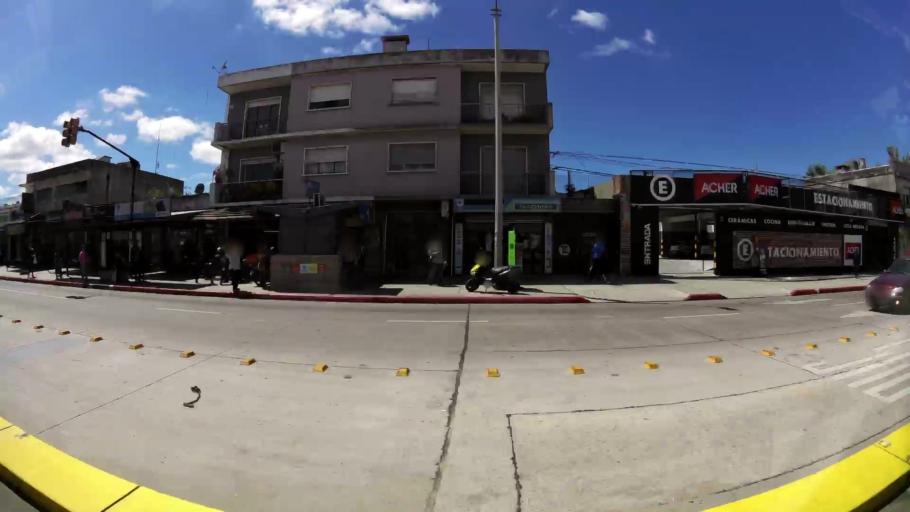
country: UY
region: Montevideo
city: Montevideo
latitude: -34.8564
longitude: -56.1326
